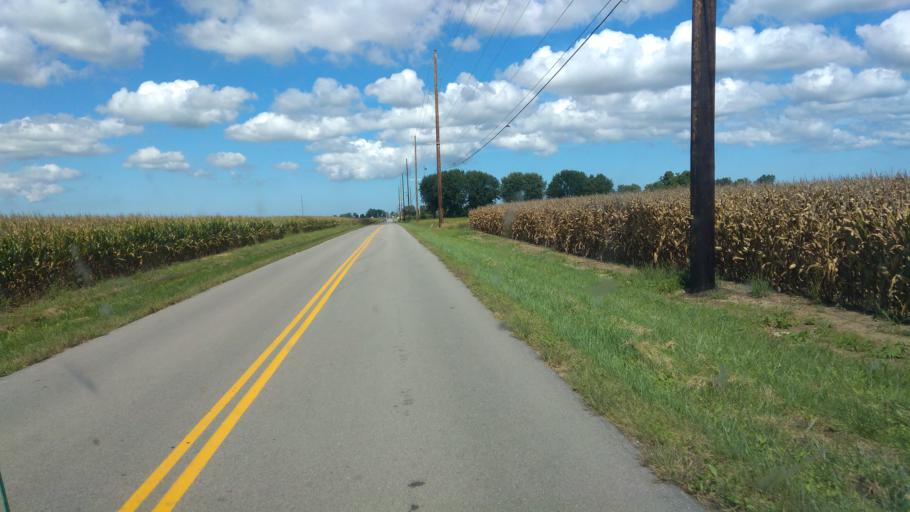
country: US
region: Ohio
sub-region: Huron County
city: Monroeville
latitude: 41.2349
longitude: -82.6654
